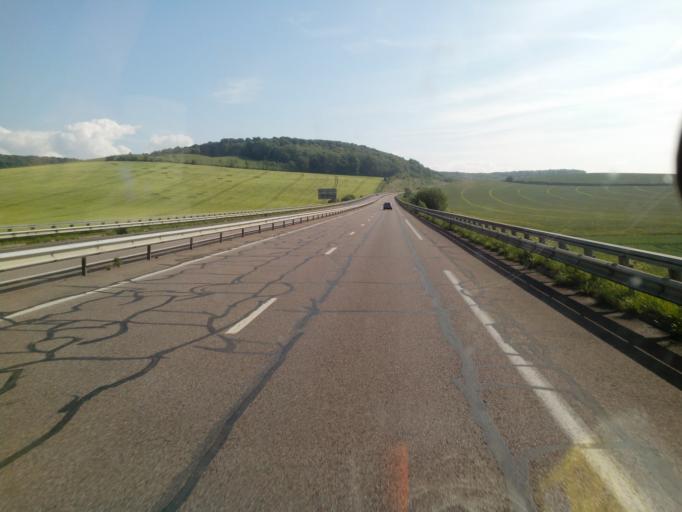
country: FR
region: Haute-Normandie
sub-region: Departement de la Seine-Maritime
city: Blangy-sur-Bresle
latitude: 49.9201
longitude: 1.6356
